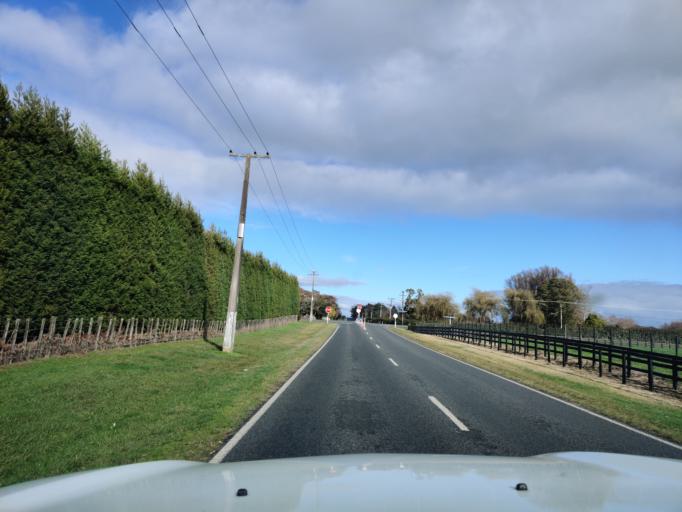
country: NZ
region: Waikato
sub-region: Waipa District
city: Cambridge
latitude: -37.8592
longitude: 175.4391
